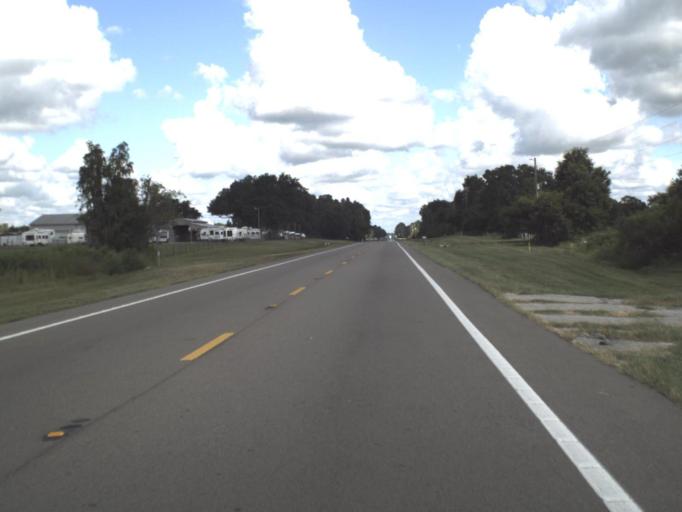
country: US
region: Florida
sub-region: Polk County
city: Kathleen
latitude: 28.2103
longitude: -82.0134
